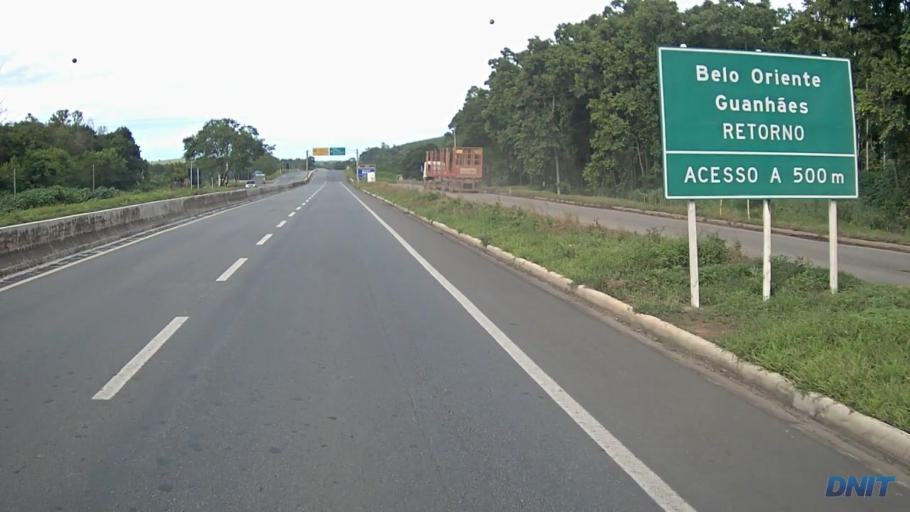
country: BR
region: Minas Gerais
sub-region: Ipaba
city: Ipaba
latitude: -19.3118
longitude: -42.3948
